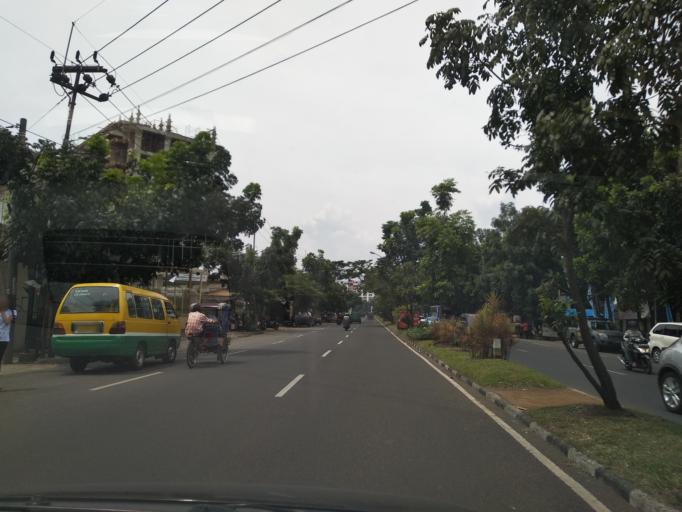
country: ID
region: West Java
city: Bandung
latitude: -6.9325
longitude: 107.5898
